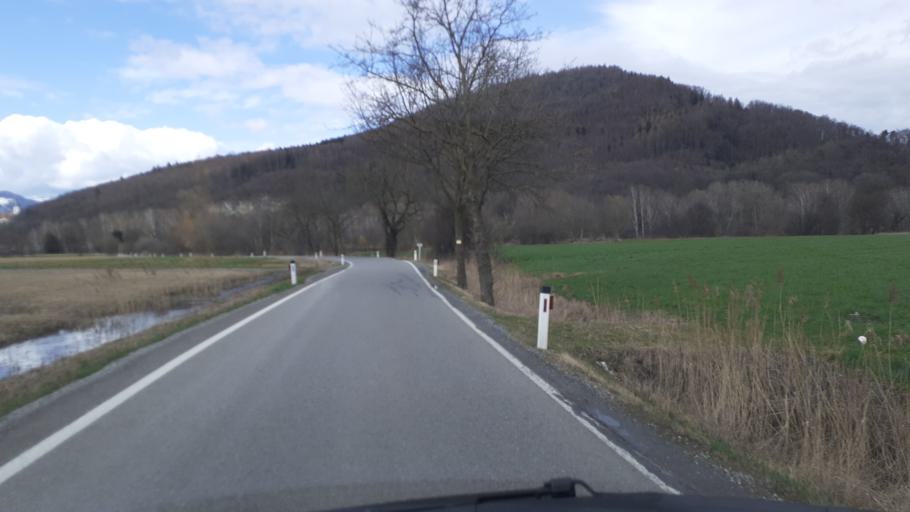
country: AT
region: Vorarlberg
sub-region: Politischer Bezirk Feldkirch
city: Koblach
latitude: 47.3248
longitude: 9.6160
